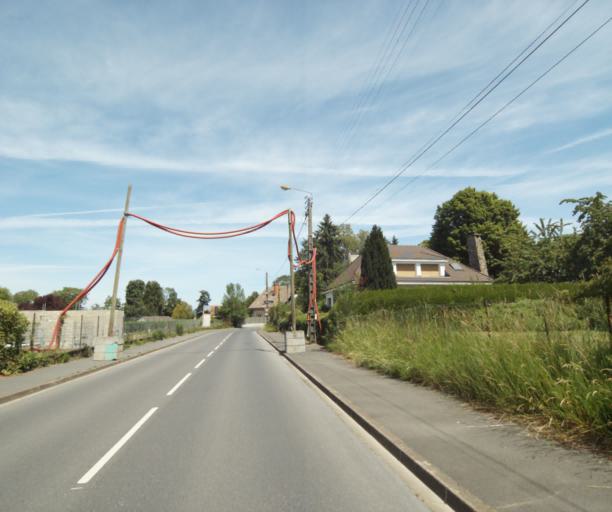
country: FR
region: Champagne-Ardenne
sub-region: Departement des Ardennes
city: Charleville-Mezieres
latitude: 49.7536
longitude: 4.7160
